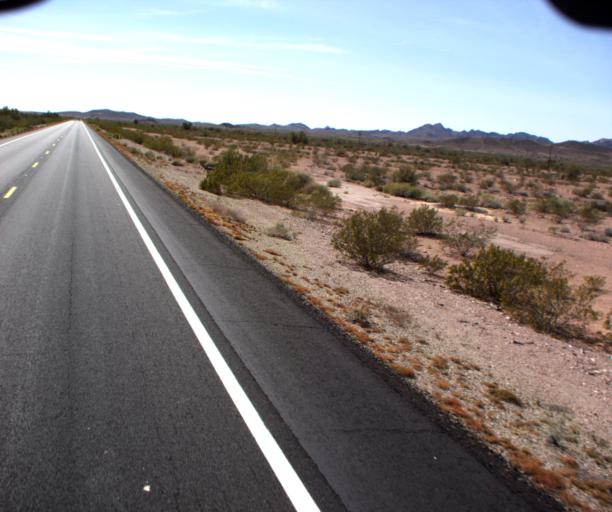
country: US
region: Arizona
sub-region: La Paz County
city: Quartzsite
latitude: 33.2819
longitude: -114.2306
